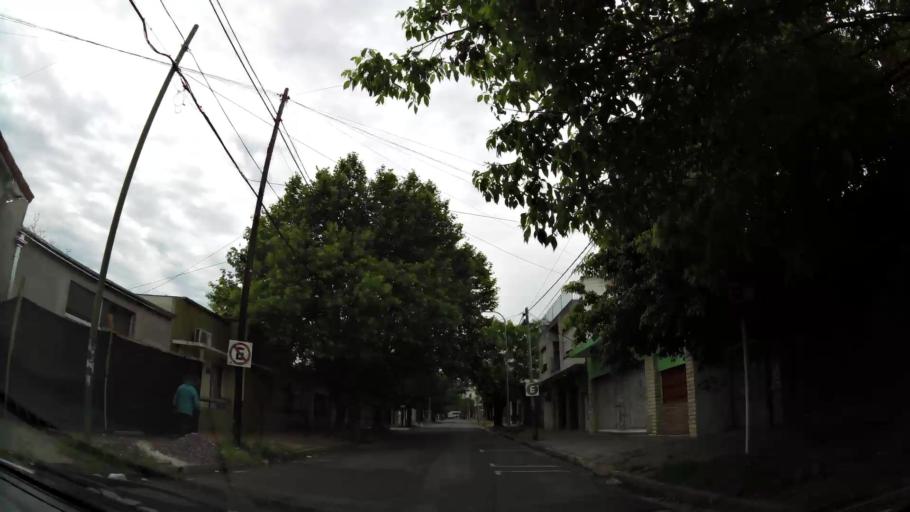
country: AR
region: Buenos Aires
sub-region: Partido de Quilmes
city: Quilmes
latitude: -34.7573
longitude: -58.2111
